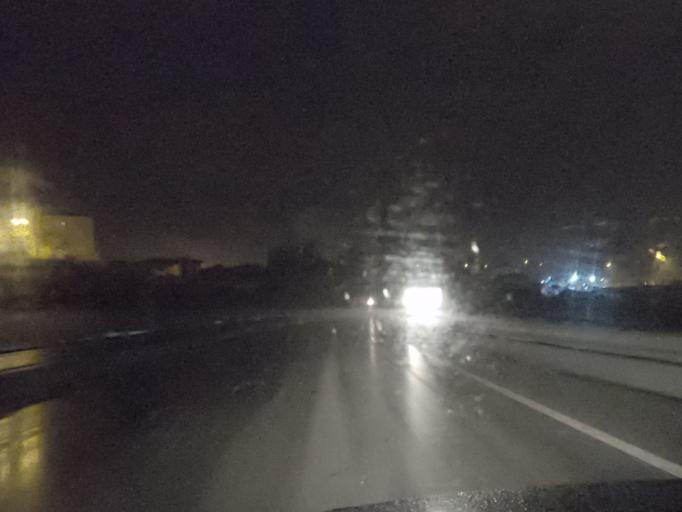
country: PT
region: Vila Real
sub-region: Vila Real
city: Vila Real
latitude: 41.2848
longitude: -7.7301
